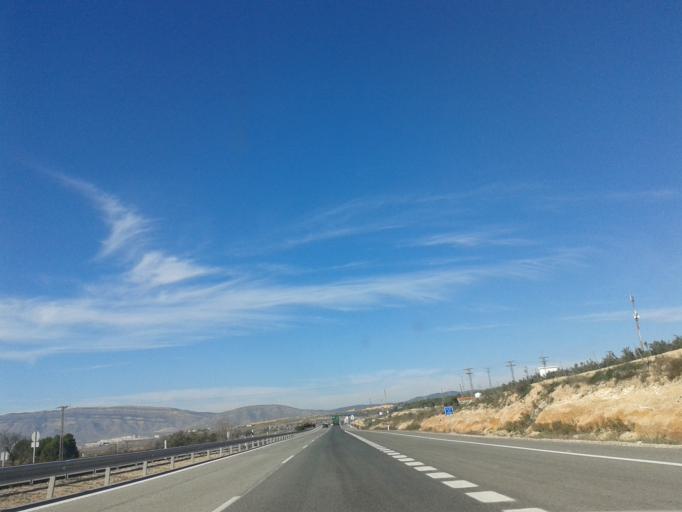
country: ES
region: Castille-La Mancha
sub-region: Provincia de Albacete
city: Caudete
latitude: 38.6985
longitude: -0.9182
